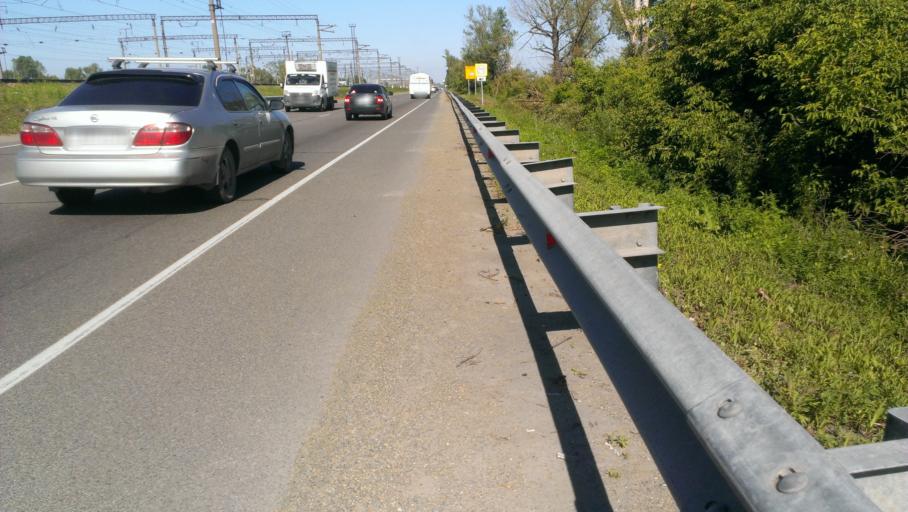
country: RU
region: Altai Krai
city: Novoaltaysk
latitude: 53.3695
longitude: 83.8636
